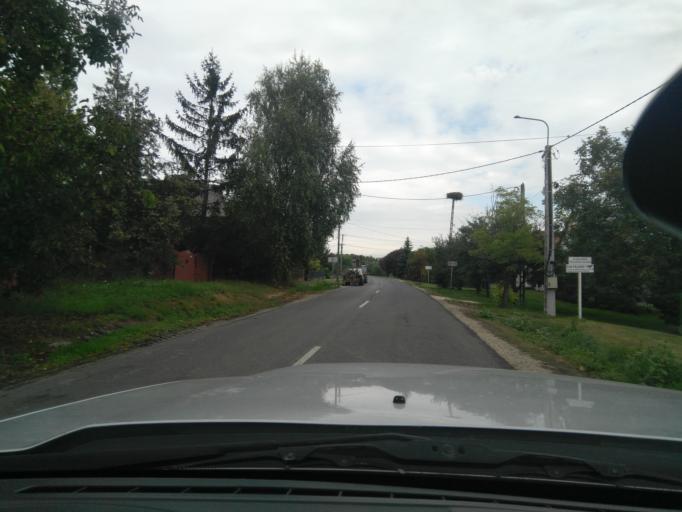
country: HU
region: Fejer
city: Val
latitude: 47.3602
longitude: 18.7362
